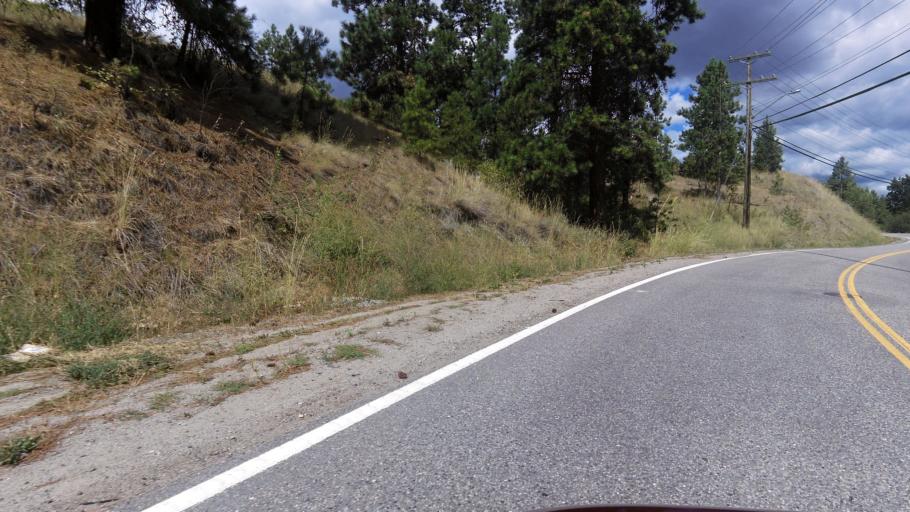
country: CA
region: British Columbia
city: West Kelowna
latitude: 49.8256
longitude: -119.6180
